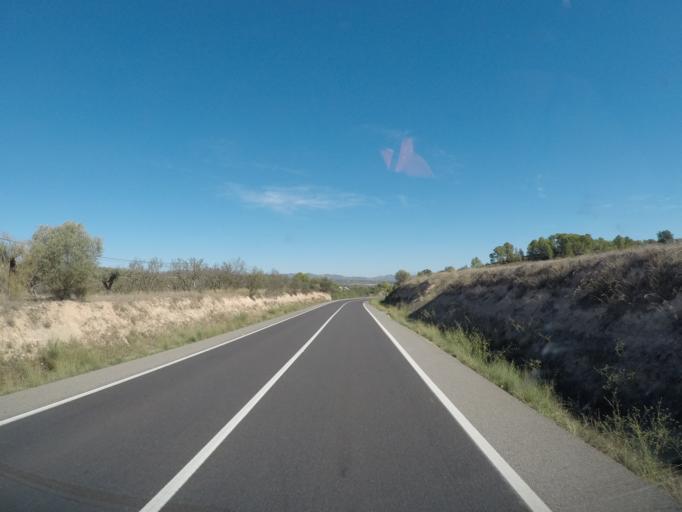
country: ES
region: Catalonia
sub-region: Provincia de Tarragona
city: Miravet
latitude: 41.0286
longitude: 0.6040
